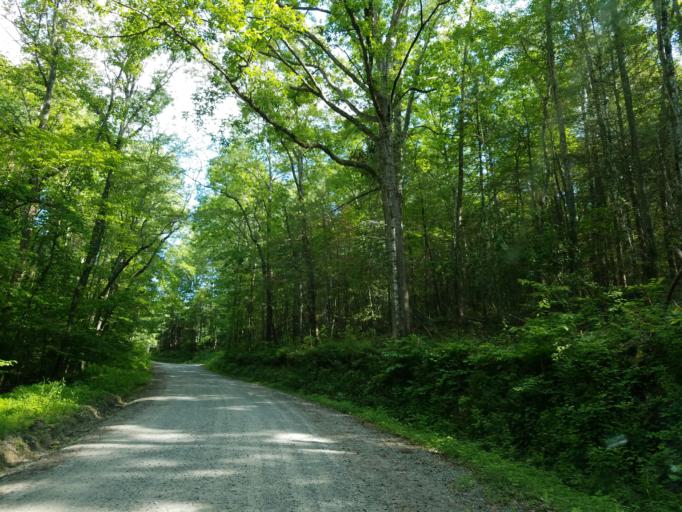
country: US
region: Georgia
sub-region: Fannin County
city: Blue Ridge
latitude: 34.8006
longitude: -84.2457
